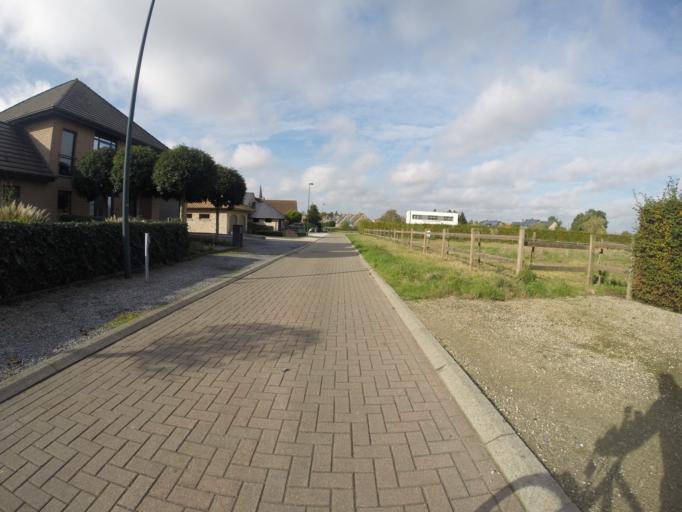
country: BE
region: Flanders
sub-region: Provincie Oost-Vlaanderen
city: Knesselare
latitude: 51.1392
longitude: 3.4188
